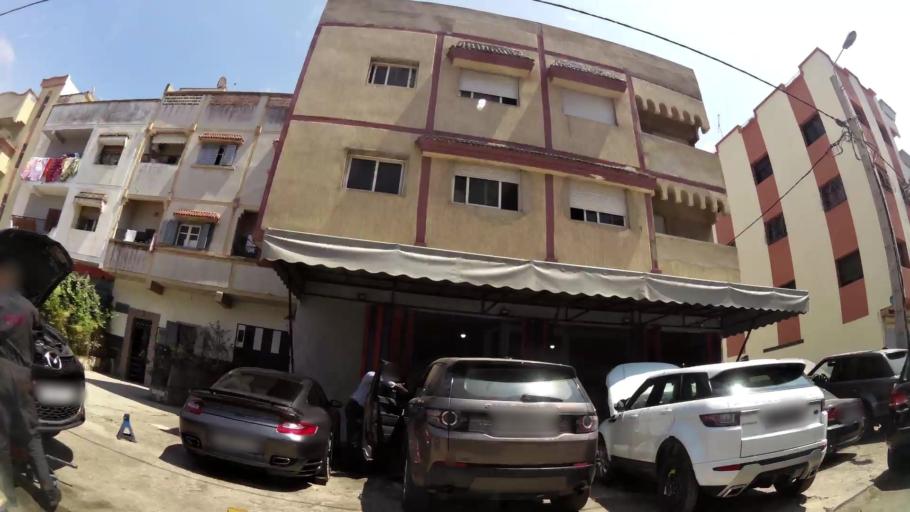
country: MA
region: Rabat-Sale-Zemmour-Zaer
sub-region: Skhirate-Temara
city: Temara
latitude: 33.9690
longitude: -6.8898
